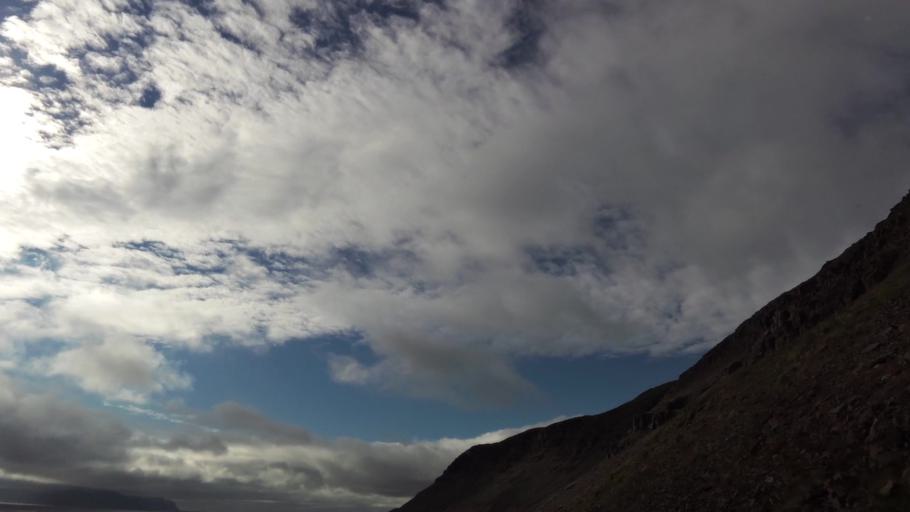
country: IS
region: West
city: Olafsvik
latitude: 65.5748
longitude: -23.9418
